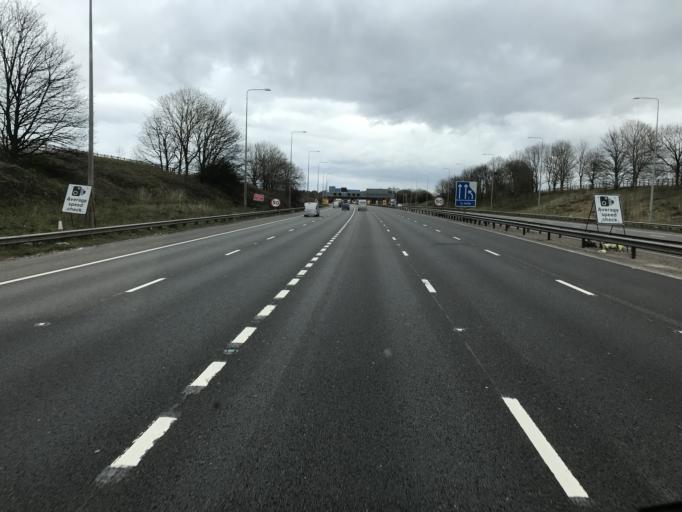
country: GB
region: England
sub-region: Warrington
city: Winwick
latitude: 53.4241
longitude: -2.5763
